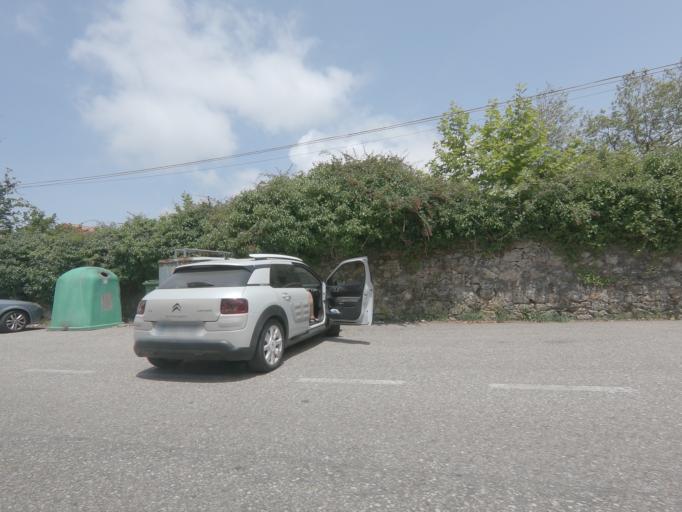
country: ES
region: Galicia
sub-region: Provincia de Pontevedra
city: A Guarda
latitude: 41.8898
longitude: -8.8524
